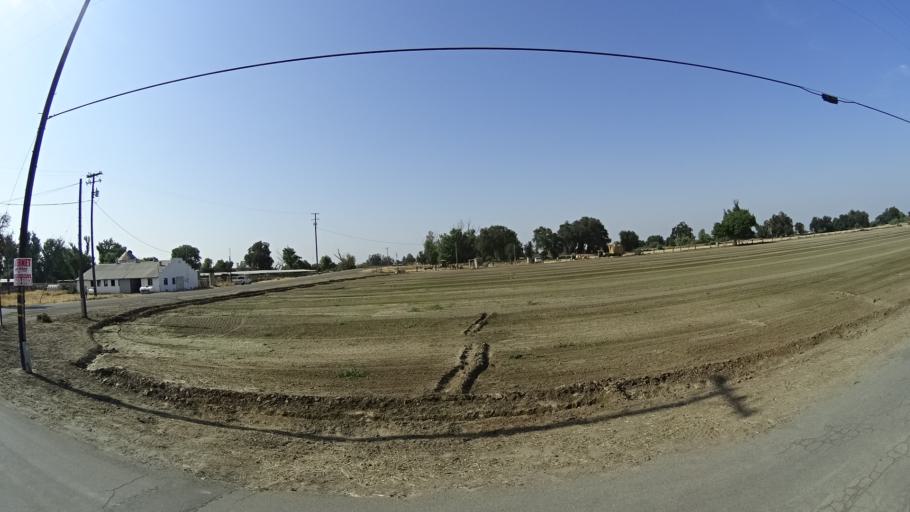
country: US
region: California
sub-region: Kings County
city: Lemoore
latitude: 36.3532
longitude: -119.8342
